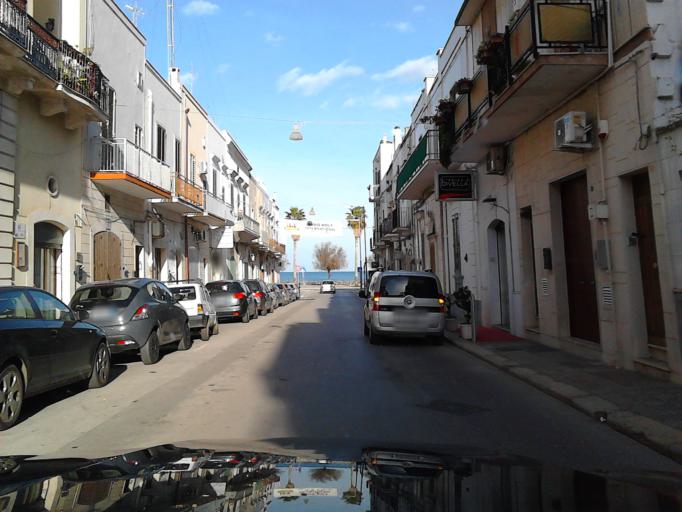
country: IT
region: Apulia
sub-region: Provincia di Bari
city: Mola di Bari
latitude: 41.0626
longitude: 17.0885
